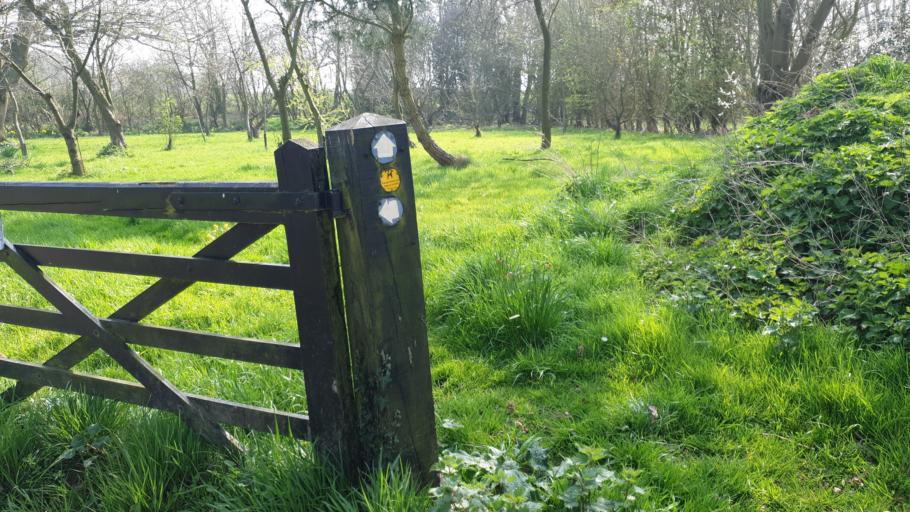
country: GB
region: England
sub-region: Essex
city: Mistley
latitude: 51.9294
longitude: 1.1629
